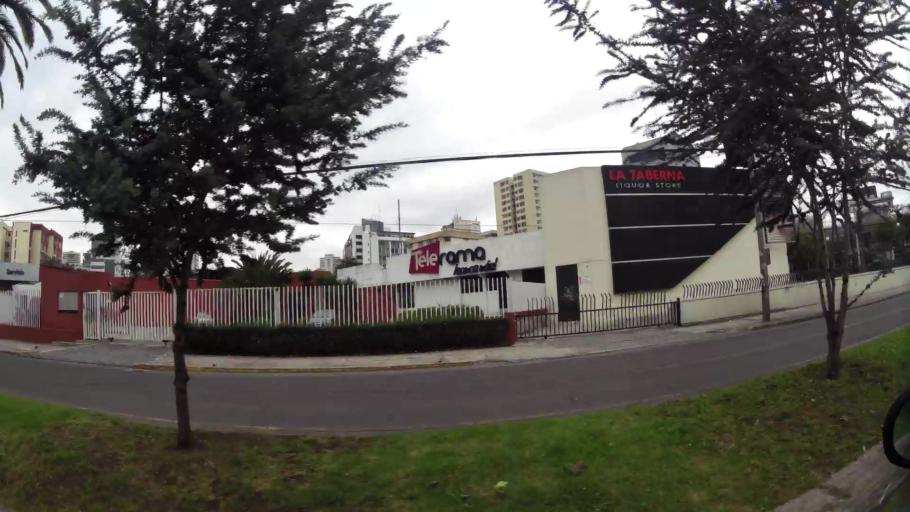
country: EC
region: Pichincha
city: Quito
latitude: -0.1978
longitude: -78.4859
